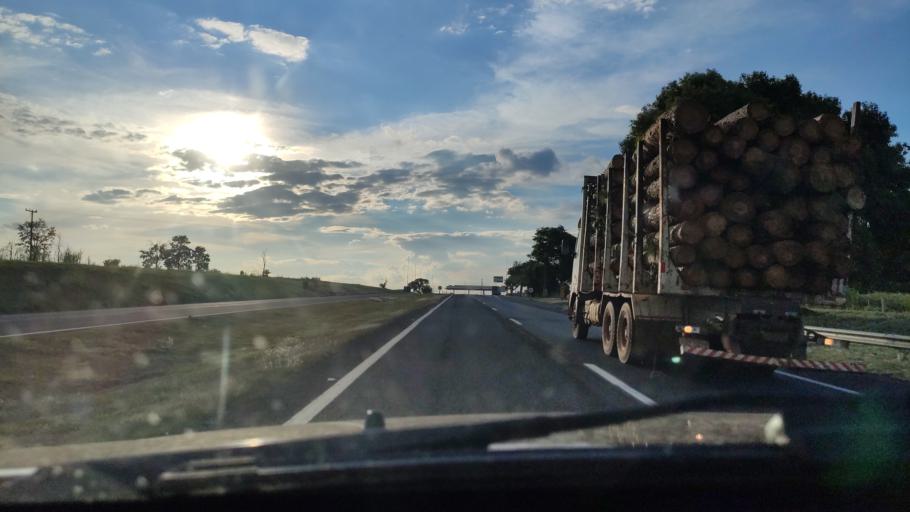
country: BR
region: Sao Paulo
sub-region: Rancharia
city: Rancharia
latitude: -22.4377
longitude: -51.0043
